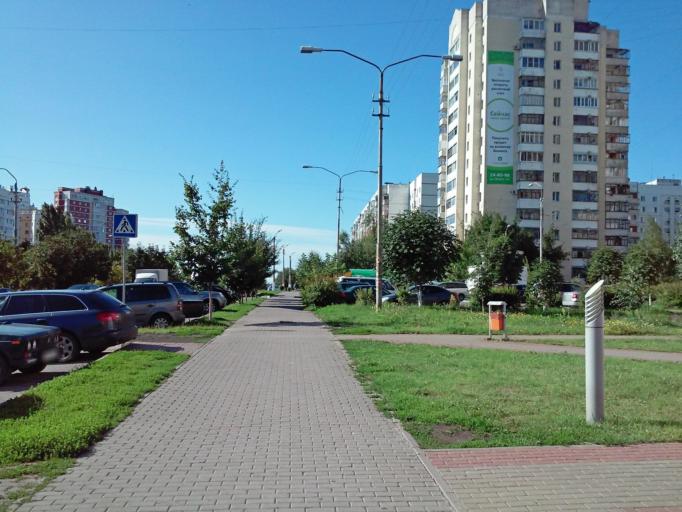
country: RU
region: Belgorod
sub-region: Belgorodskiy Rayon
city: Belgorod
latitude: 50.5584
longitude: 36.5713
